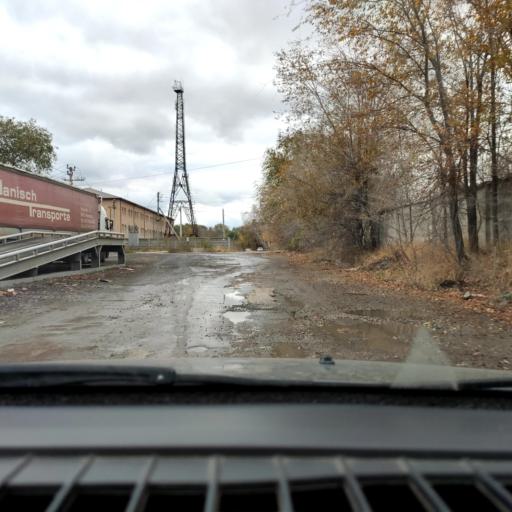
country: RU
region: Samara
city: Tol'yatti
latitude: 53.5712
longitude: 49.2827
